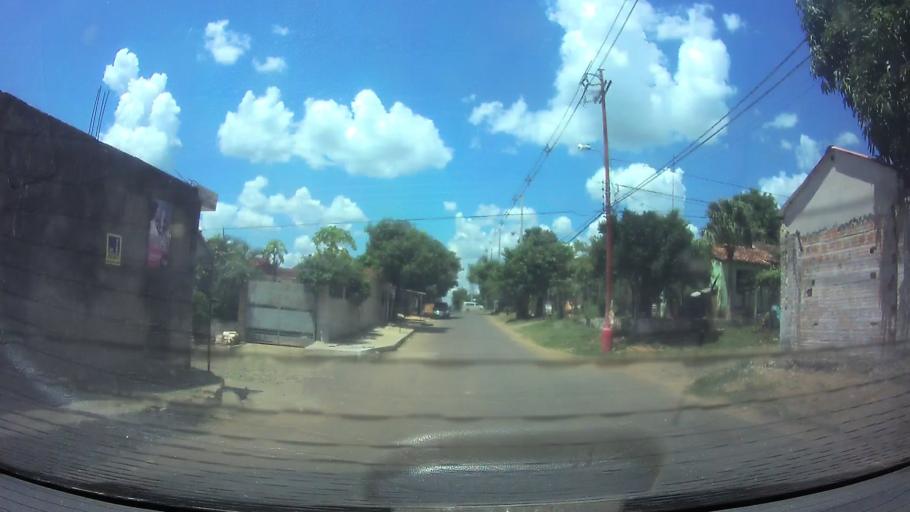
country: PY
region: Central
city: Limpio
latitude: -25.1527
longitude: -57.4495
